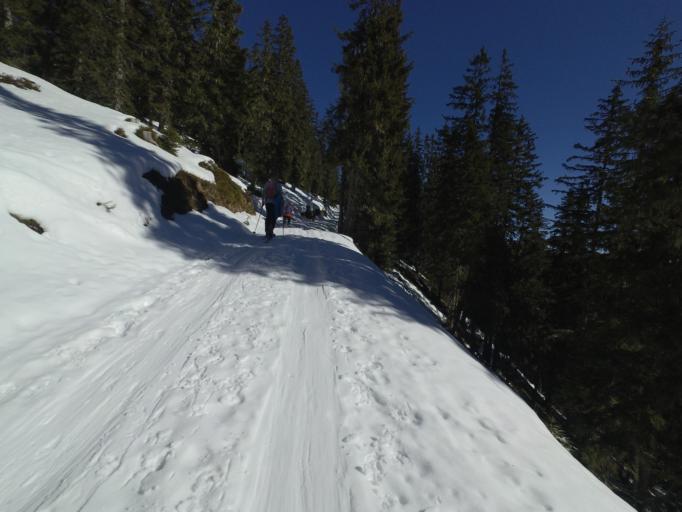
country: AT
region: Salzburg
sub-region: Politischer Bezirk Sankt Johann im Pongau
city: Muhlbach am Hochkonig
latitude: 47.3992
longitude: 13.1329
